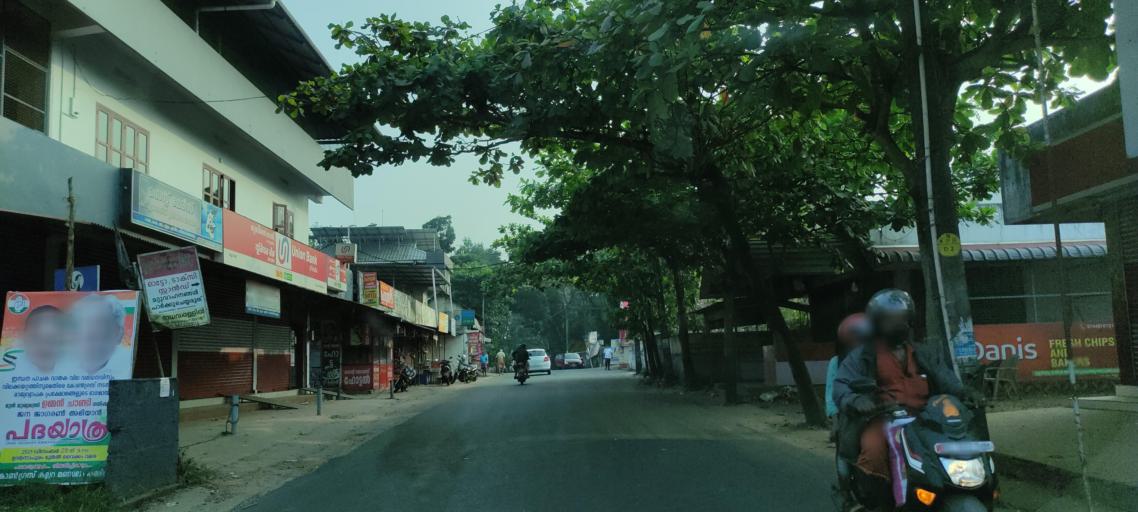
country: IN
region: Kerala
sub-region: Kottayam
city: Vaikam
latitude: 9.6976
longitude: 76.4779
